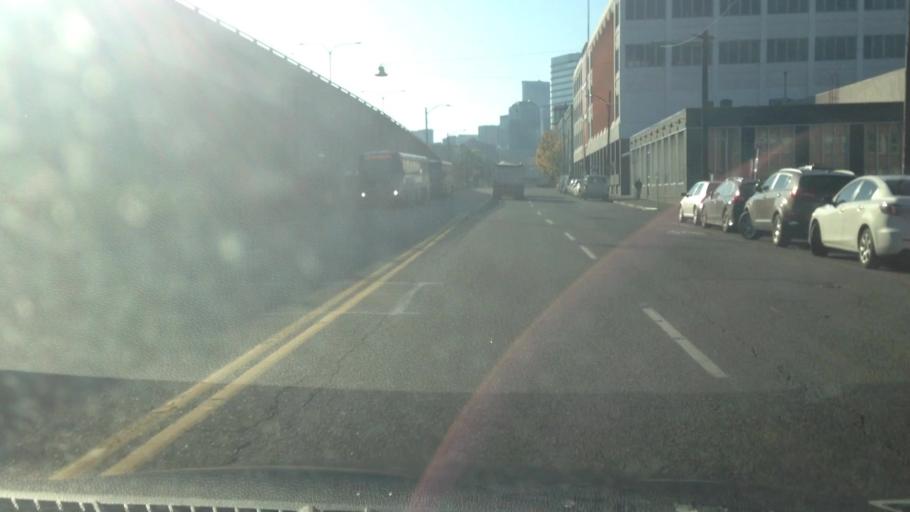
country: US
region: Washington
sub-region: King County
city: Seattle
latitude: 47.6225
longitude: -122.3292
